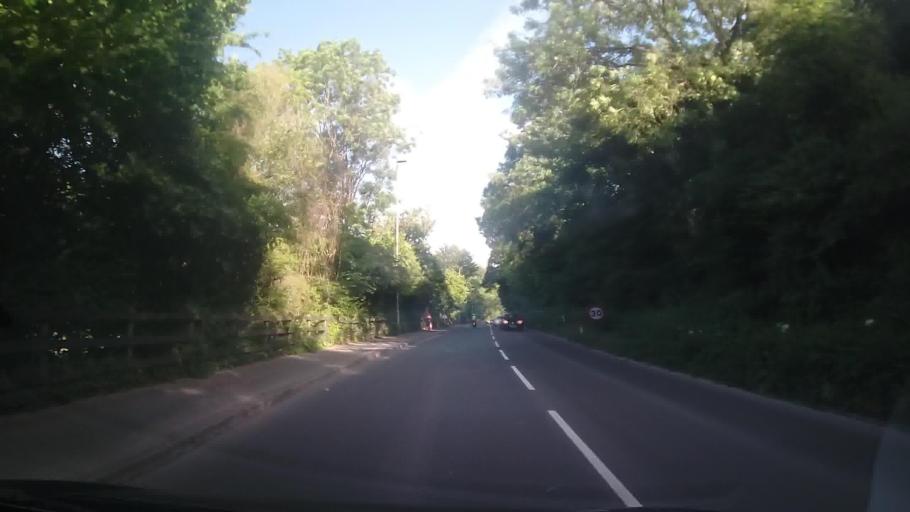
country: GB
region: England
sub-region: Devon
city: Plympton
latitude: 50.4008
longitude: -4.1000
